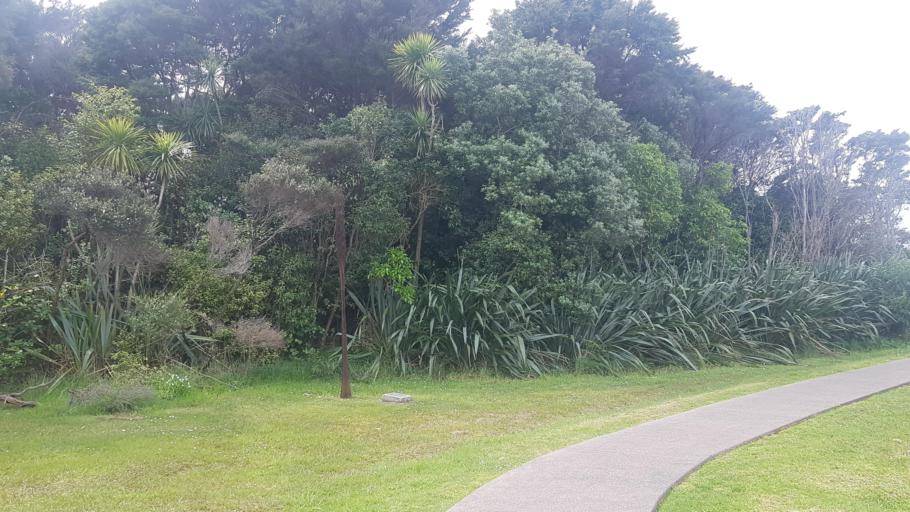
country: NZ
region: Auckland
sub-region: Auckland
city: Pakuranga
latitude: -36.7837
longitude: 175.0052
